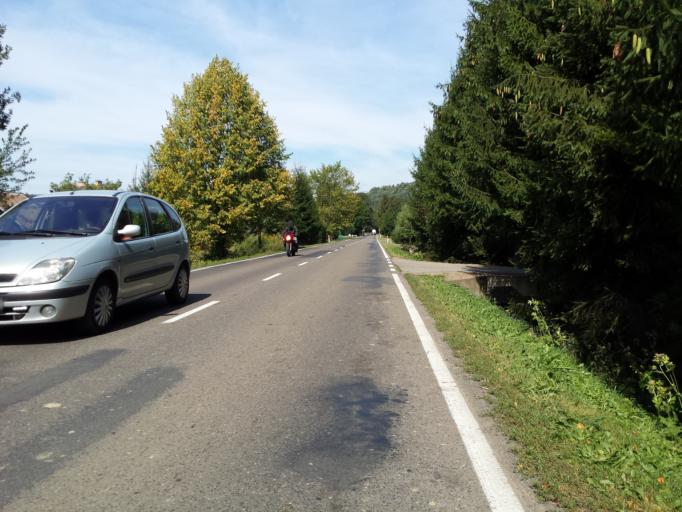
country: PL
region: Subcarpathian Voivodeship
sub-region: Powiat leski
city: Lesko
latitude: 49.4522
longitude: 22.3443
